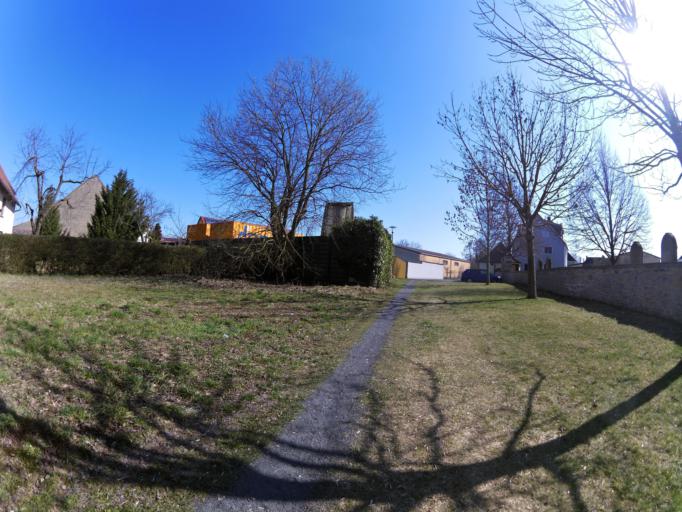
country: DE
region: Bavaria
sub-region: Regierungsbezirk Unterfranken
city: Oberpleichfeld
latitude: 49.8777
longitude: 10.0832
